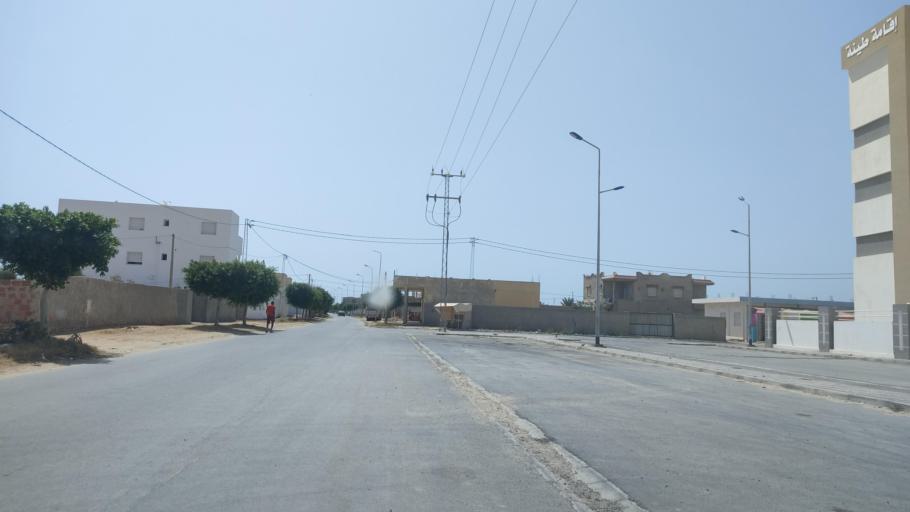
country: TN
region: Safaqis
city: Sfax
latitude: 34.6688
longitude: 10.7069
